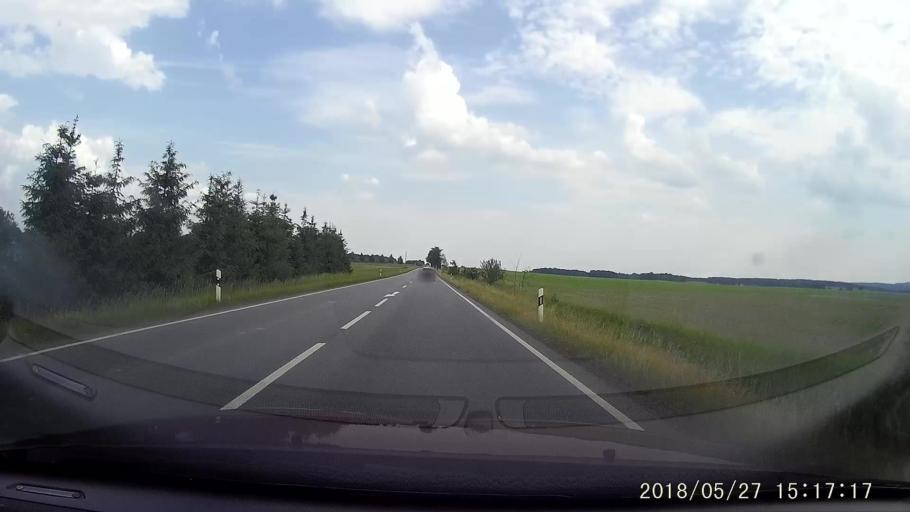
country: DE
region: Saxony
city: Niesky
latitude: 51.2720
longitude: 14.8390
